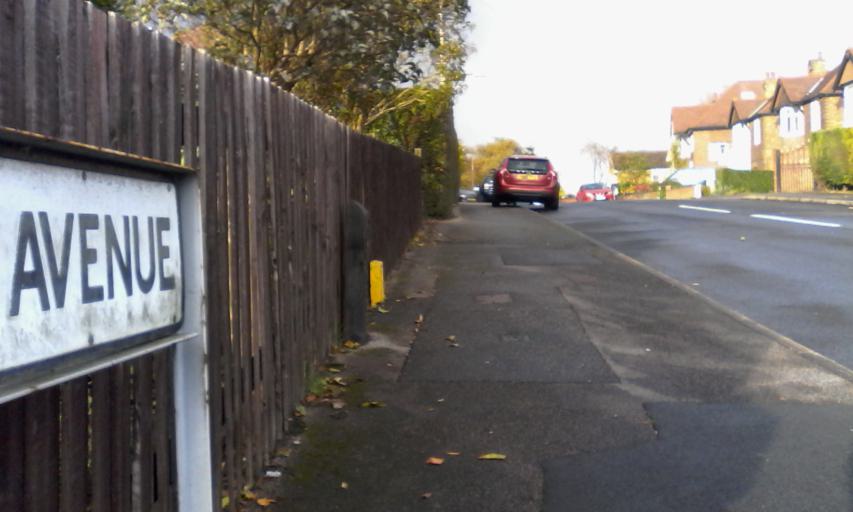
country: GB
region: England
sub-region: Nottinghamshire
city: Arnold
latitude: 52.9798
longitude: -1.1009
